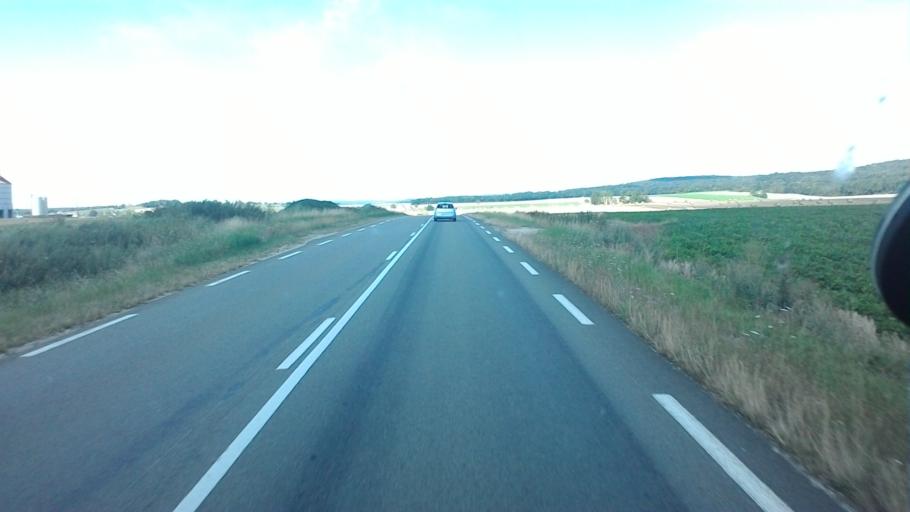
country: FR
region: Franche-Comte
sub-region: Departement de la Haute-Saone
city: Gy
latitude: 47.4469
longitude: 5.8867
